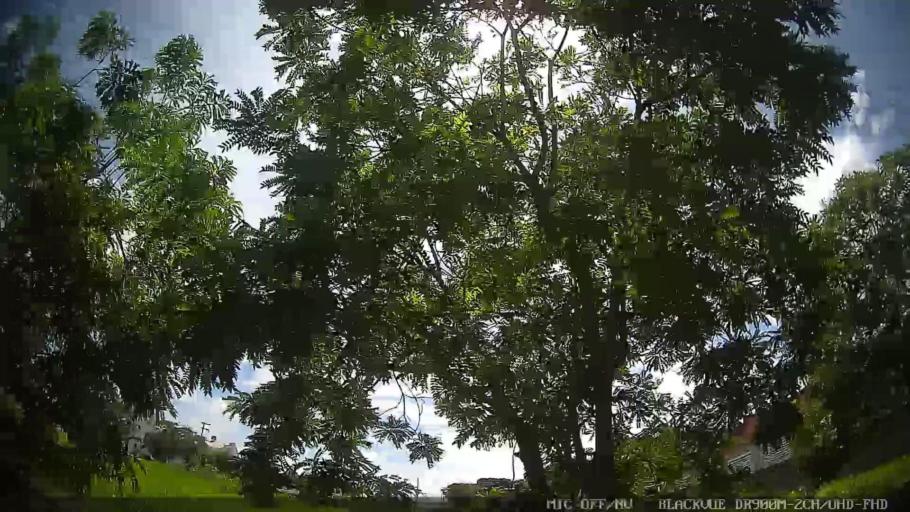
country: BR
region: Sao Paulo
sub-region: Jaguariuna
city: Jaguariuna
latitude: -22.6152
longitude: -47.0601
